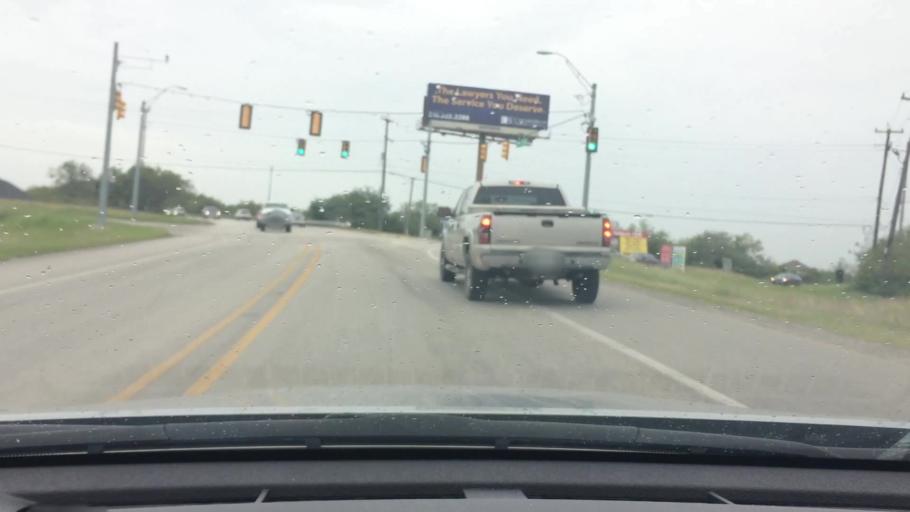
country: US
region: Texas
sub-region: Bexar County
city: Converse
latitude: 29.4775
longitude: -98.3140
